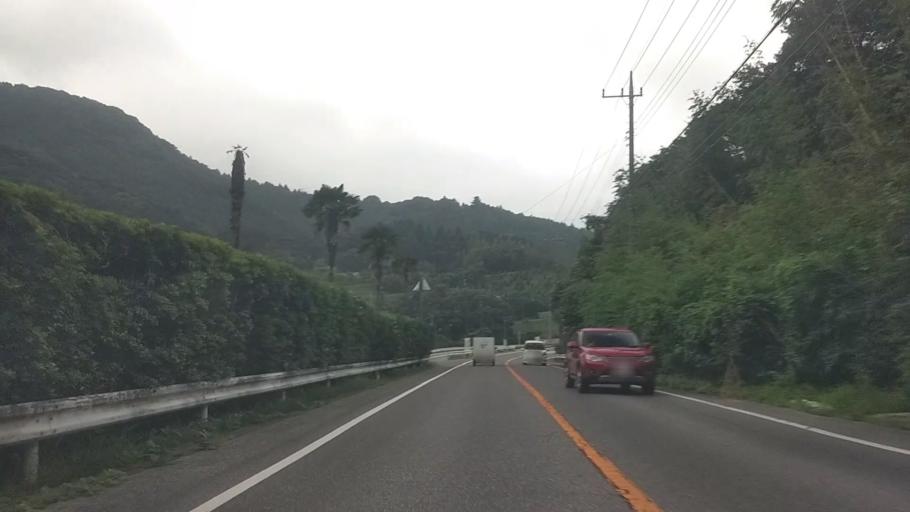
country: JP
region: Chiba
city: Kawaguchi
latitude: 35.1447
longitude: 140.0691
